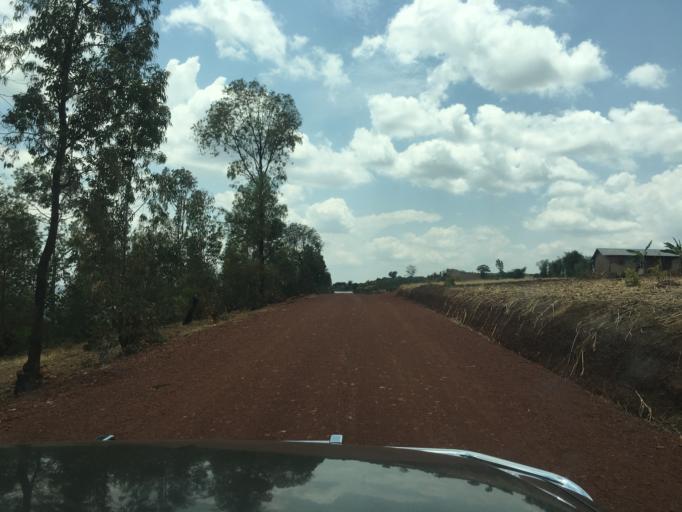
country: RW
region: Eastern Province
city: Kibungo
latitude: -2.2385
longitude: 30.7536
